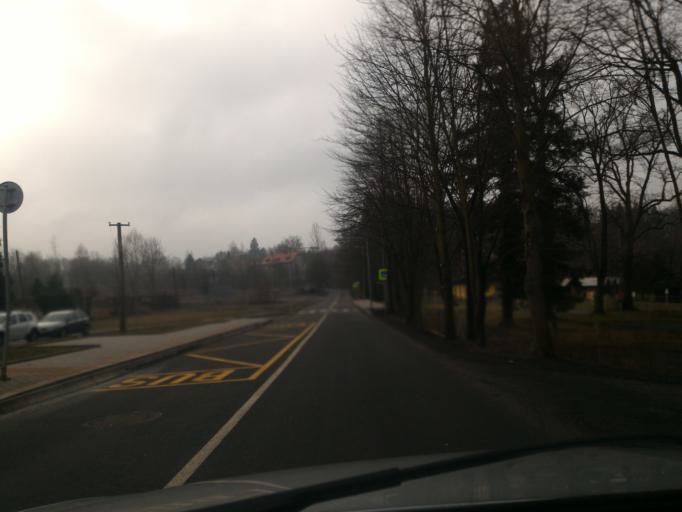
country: CZ
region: Liberecky
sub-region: Okres Liberec
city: Frydlant
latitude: 50.9142
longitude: 15.0865
